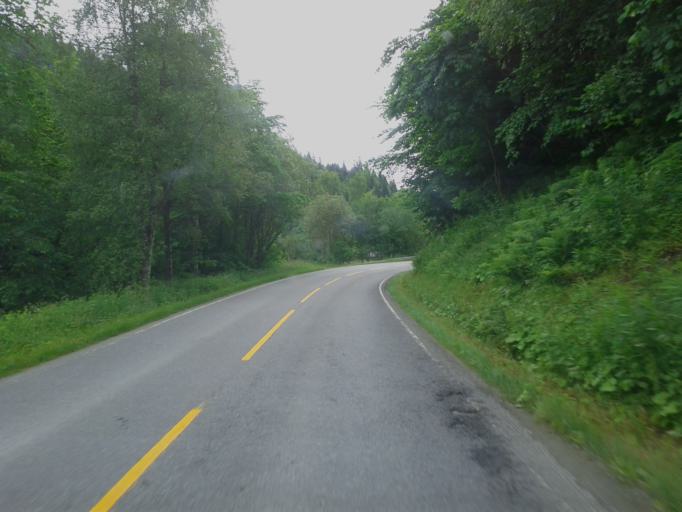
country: NO
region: Sor-Trondelag
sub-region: Midtre Gauldal
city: Storen
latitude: 62.9998
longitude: 10.4626
